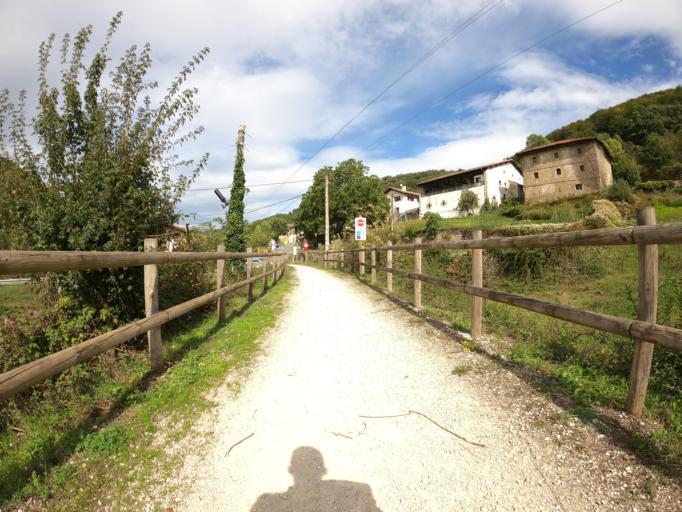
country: ES
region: Navarre
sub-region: Provincia de Navarra
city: Irurtzun
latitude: 42.9536
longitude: -1.8235
